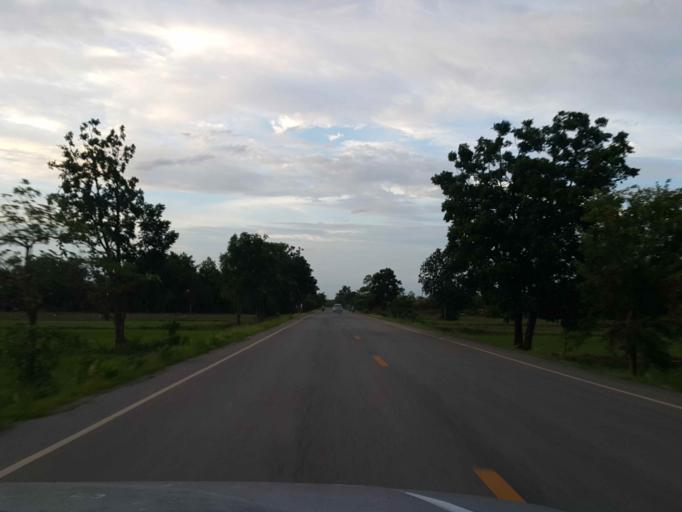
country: TH
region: Sukhothai
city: Ban Dan Lan Hoi
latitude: 17.0613
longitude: 99.5915
